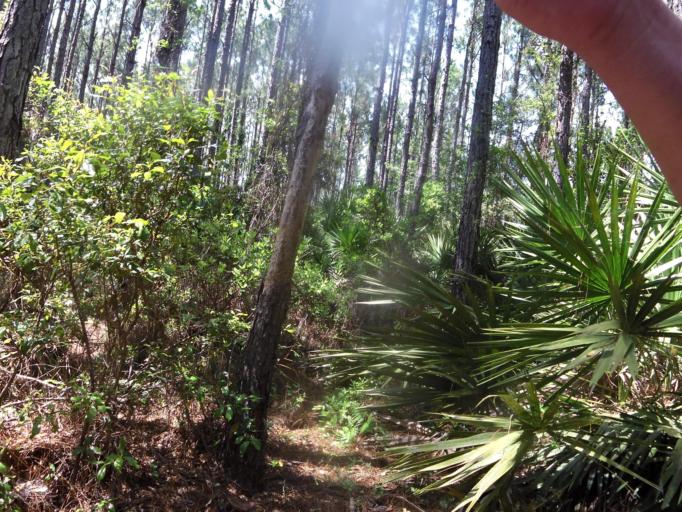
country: US
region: Florida
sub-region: Nassau County
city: Yulee
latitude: 30.4924
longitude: -81.4978
